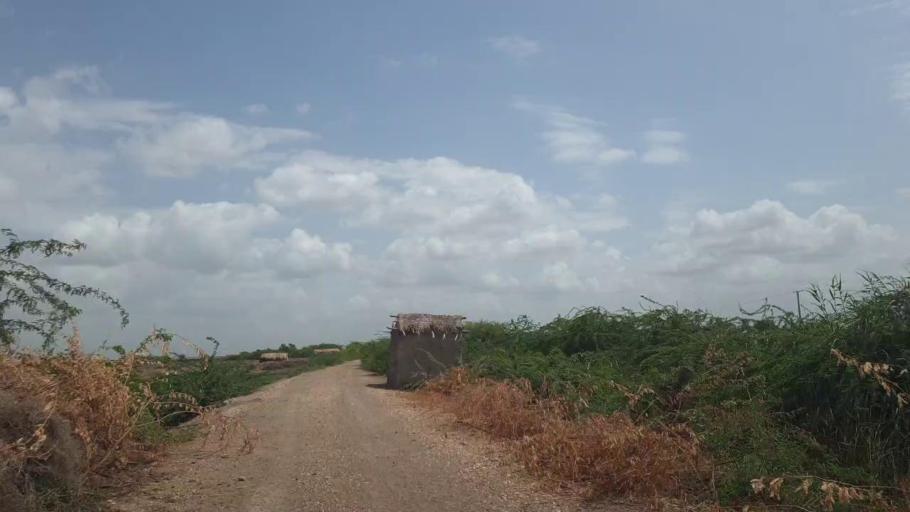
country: PK
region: Sindh
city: Tando Bago
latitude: 24.6555
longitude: 68.9928
